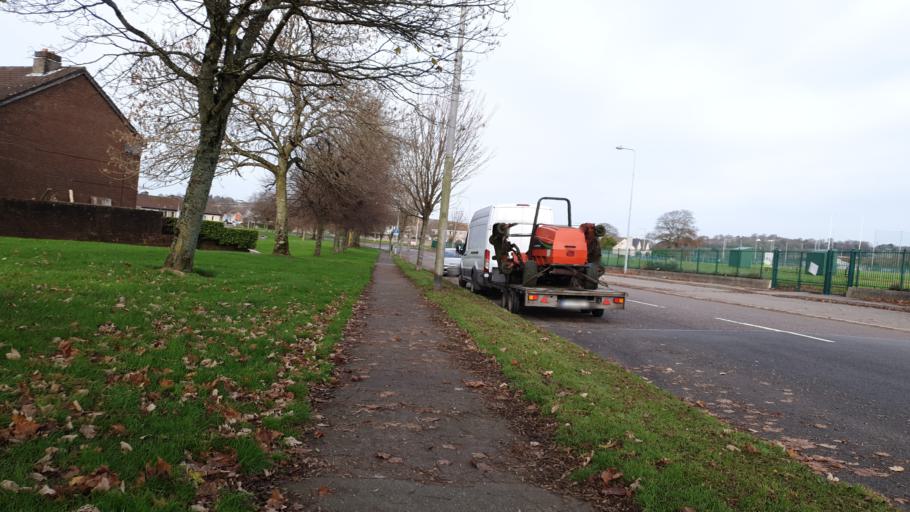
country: IE
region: Munster
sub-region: County Cork
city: Passage West
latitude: 51.8931
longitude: -8.3961
